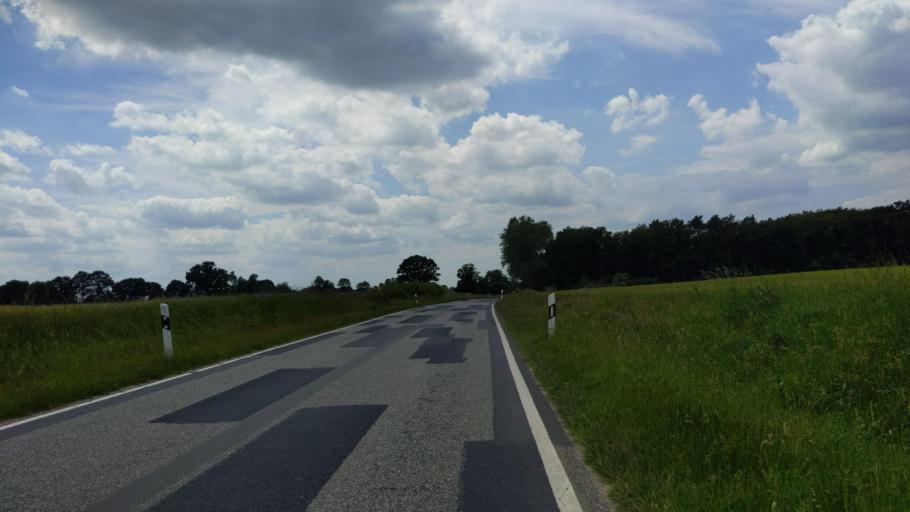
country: DE
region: Mecklenburg-Vorpommern
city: Selmsdorf
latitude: 53.8648
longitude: 10.8253
